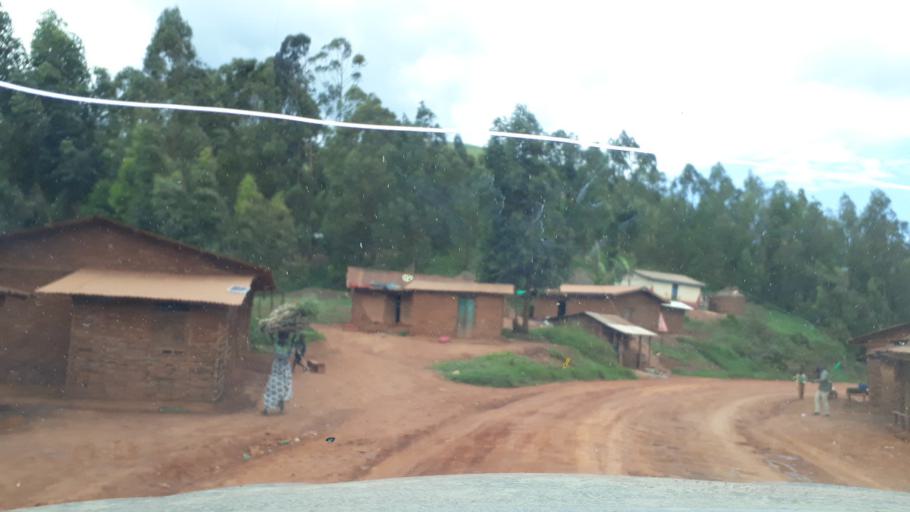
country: CD
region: Eastern Province
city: Bunia
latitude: 1.7598
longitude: 30.3614
